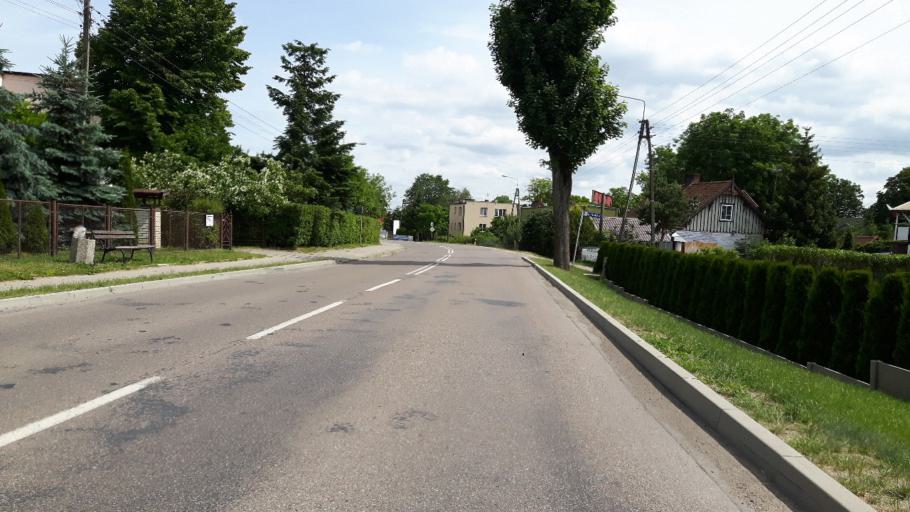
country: PL
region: Pomeranian Voivodeship
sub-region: Powiat nowodworski
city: Stegna
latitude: 54.3275
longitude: 19.1056
